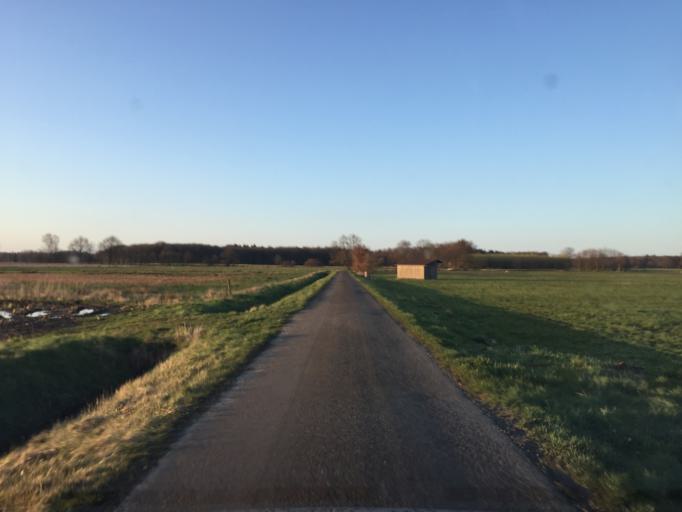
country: DE
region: Lower Saxony
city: Varrel
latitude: 52.6601
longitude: 8.7472
